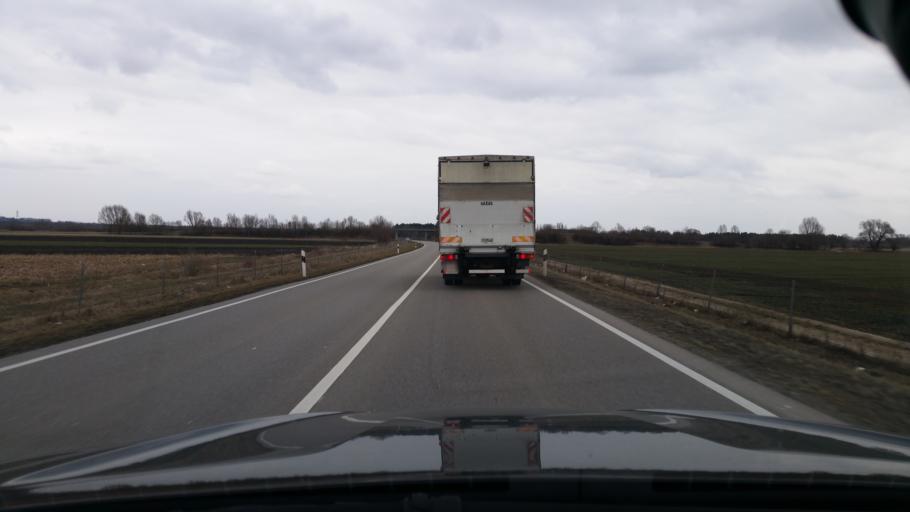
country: DE
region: Bavaria
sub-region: Upper Bavaria
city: Eitting
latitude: 48.3748
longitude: 11.8569
